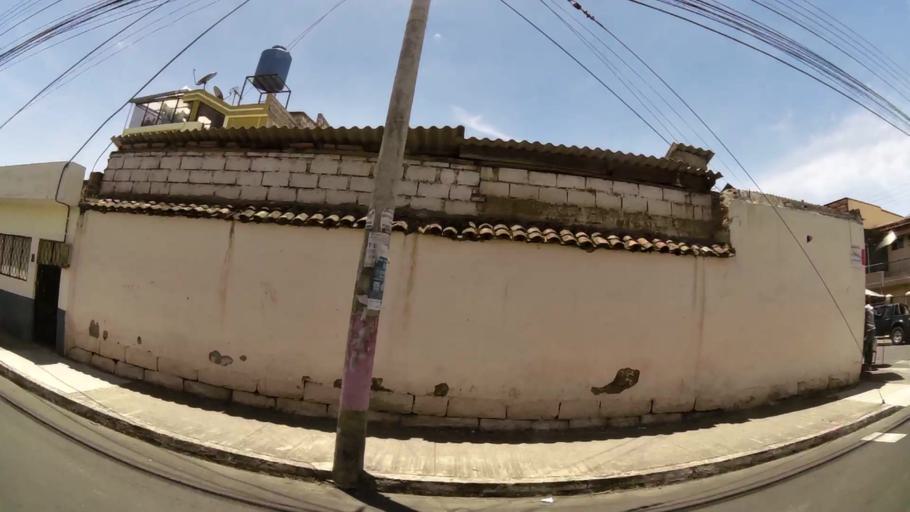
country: EC
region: Chimborazo
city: Riobamba
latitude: -1.6649
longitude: -78.6510
